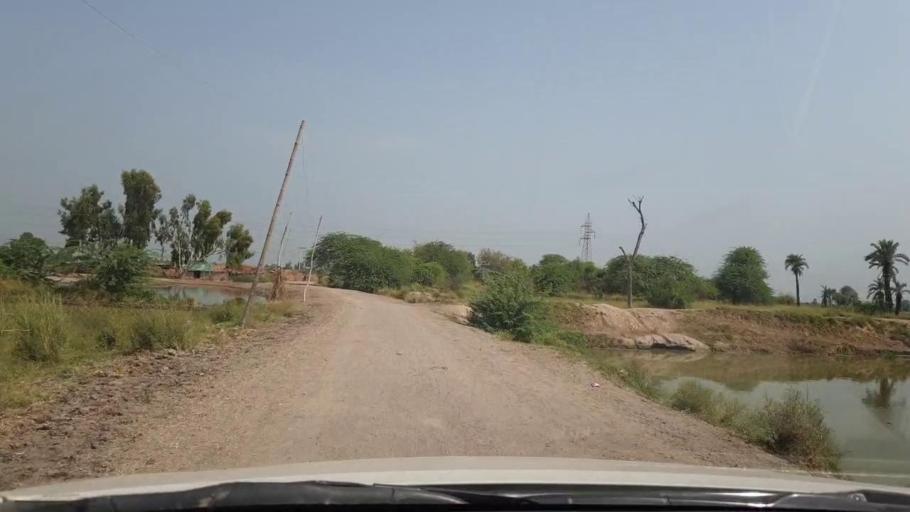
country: PK
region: Sindh
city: Shikarpur
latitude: 27.9719
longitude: 68.6708
